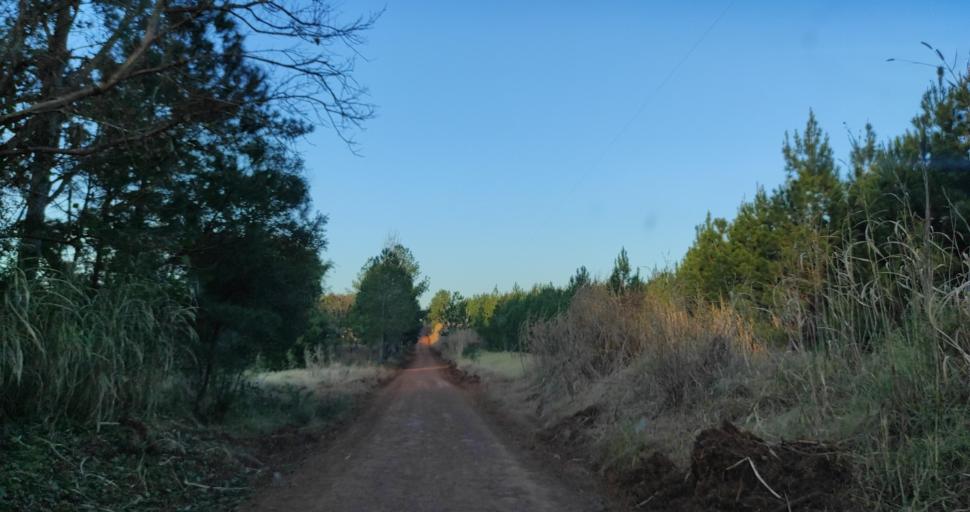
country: AR
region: Misiones
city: Capiovi
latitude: -26.8808
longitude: -55.1151
